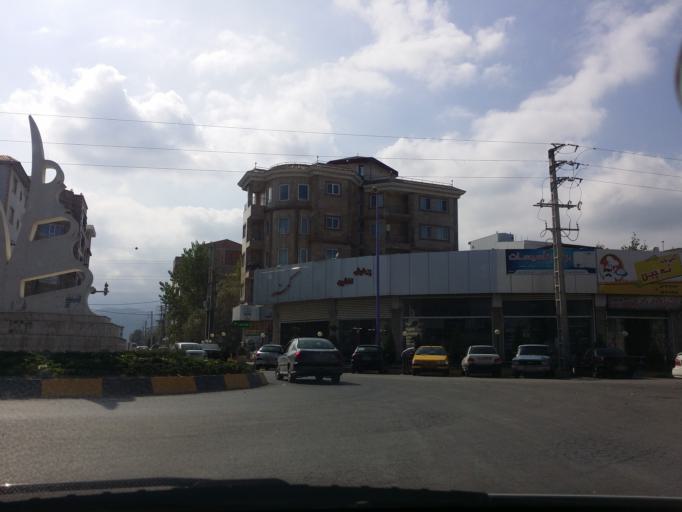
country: IR
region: Mazandaran
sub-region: Nowshahr
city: Nowshahr
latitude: 36.6504
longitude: 51.4857
